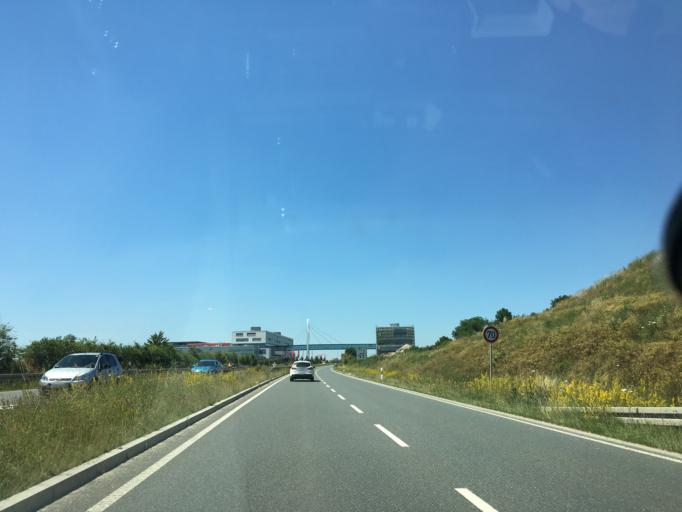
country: DE
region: Bavaria
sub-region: Regierungsbezirk Mittelfranken
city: Herzogenaurach
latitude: 49.5733
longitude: 10.9069
